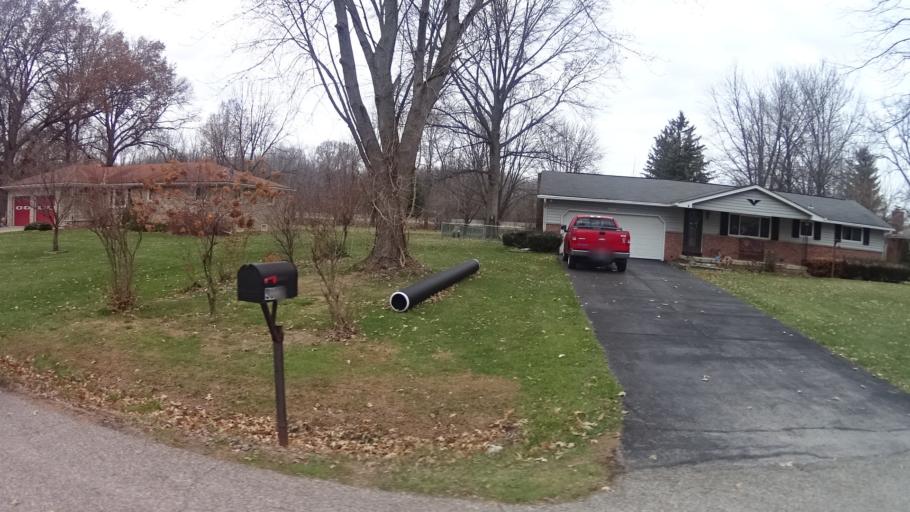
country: US
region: Ohio
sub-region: Lorain County
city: North Ridgeville
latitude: 41.3787
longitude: -82.0201
